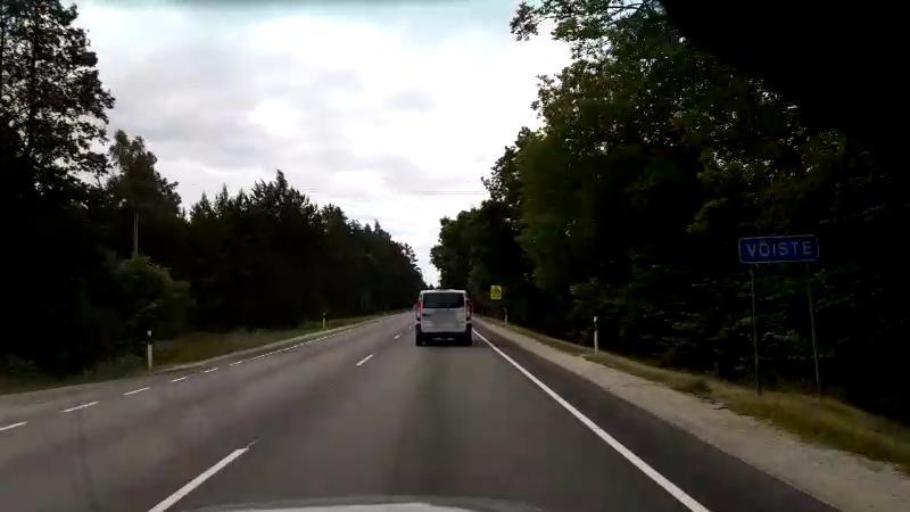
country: EE
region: Paernumaa
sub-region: Paernu linn
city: Parnu
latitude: 58.2174
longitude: 24.4877
